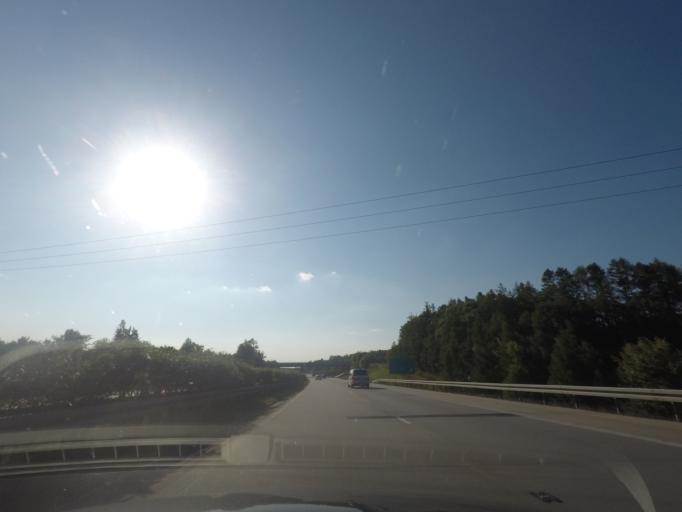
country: CZ
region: Olomoucky
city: Velky Ujezd
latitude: 49.5675
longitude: 17.4977
